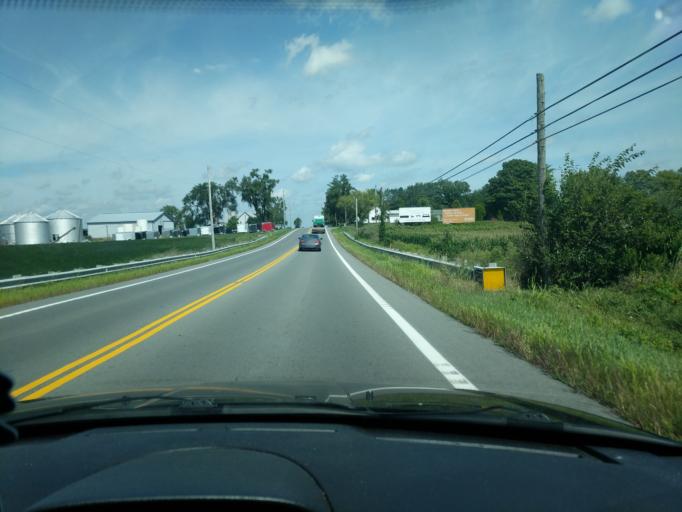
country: US
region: Ohio
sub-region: Logan County
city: Bellefontaine
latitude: 40.3084
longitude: -83.7597
